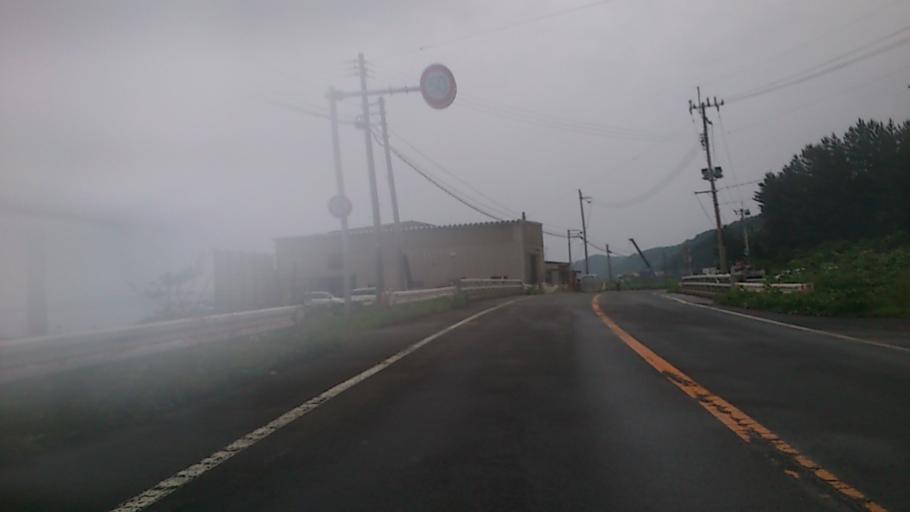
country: JP
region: Akita
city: Noshiromachi
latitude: 40.5042
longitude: 139.9498
